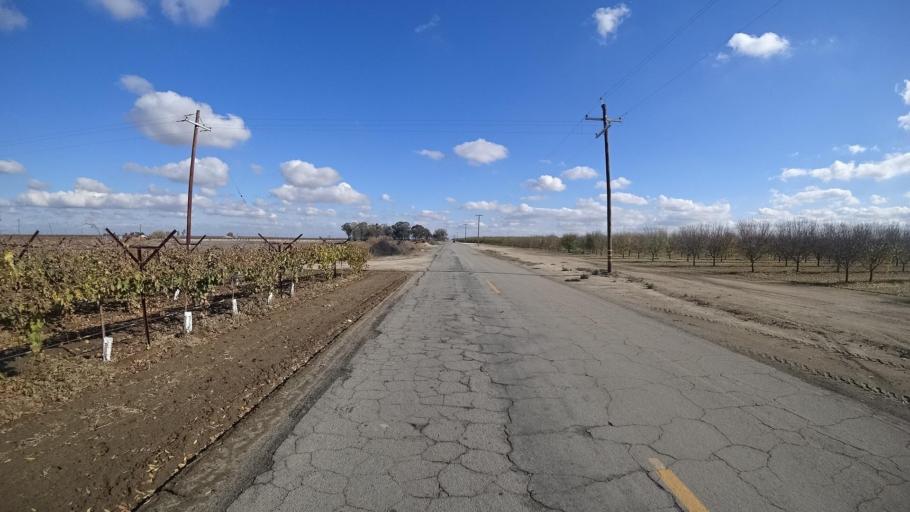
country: US
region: California
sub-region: Kern County
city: Delano
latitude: 35.7322
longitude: -119.3458
